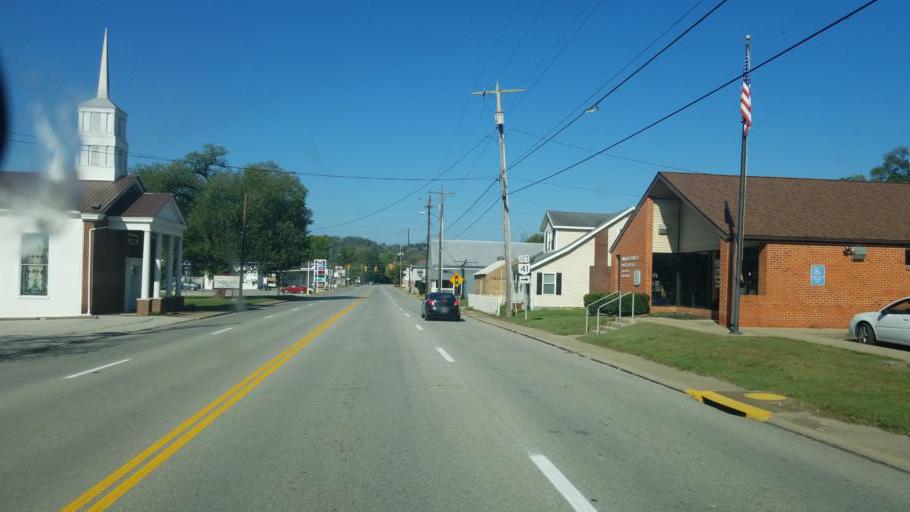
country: US
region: Ohio
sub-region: Brown County
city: Aberdeen
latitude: 38.6549
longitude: -83.7599
